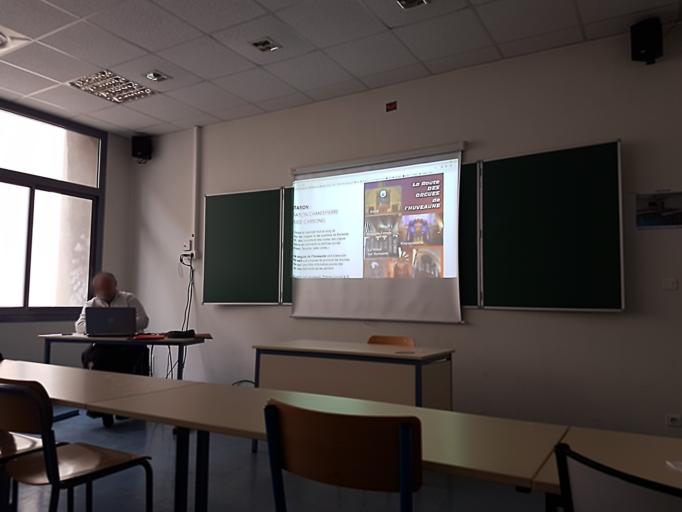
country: FR
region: Provence-Alpes-Cote d'Azur
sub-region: Departement des Bouches-du-Rhone
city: Marseille 03
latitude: 43.3065
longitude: 5.3794
